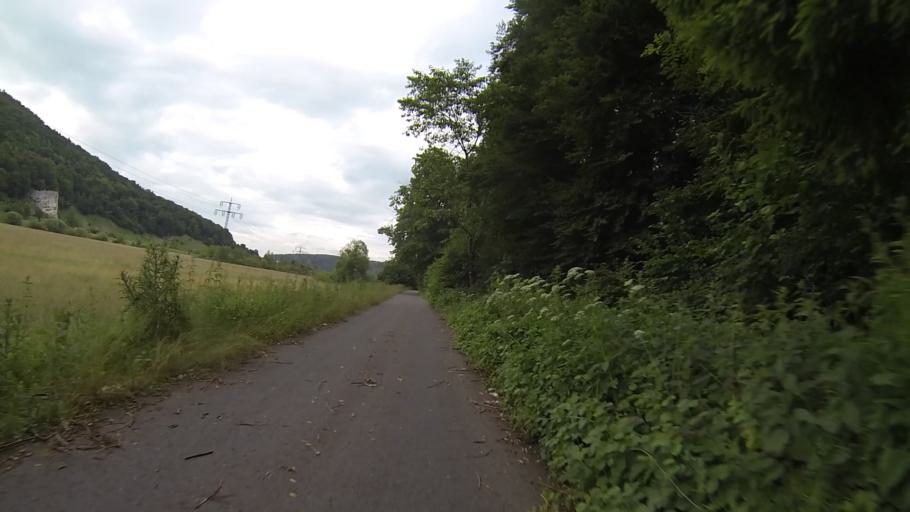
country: DE
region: Baden-Wuerttemberg
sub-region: Tuebingen Region
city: Blaubeuren
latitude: 48.4083
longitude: 9.8432
